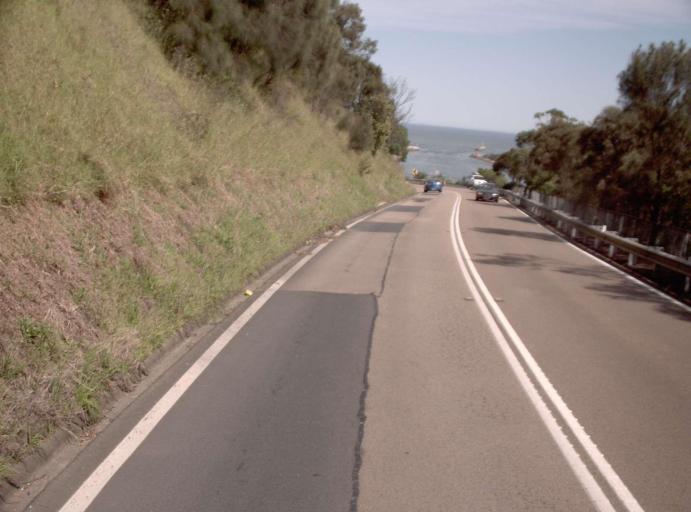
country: AU
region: Victoria
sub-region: East Gippsland
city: Lakes Entrance
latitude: -37.8807
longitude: 147.9635
